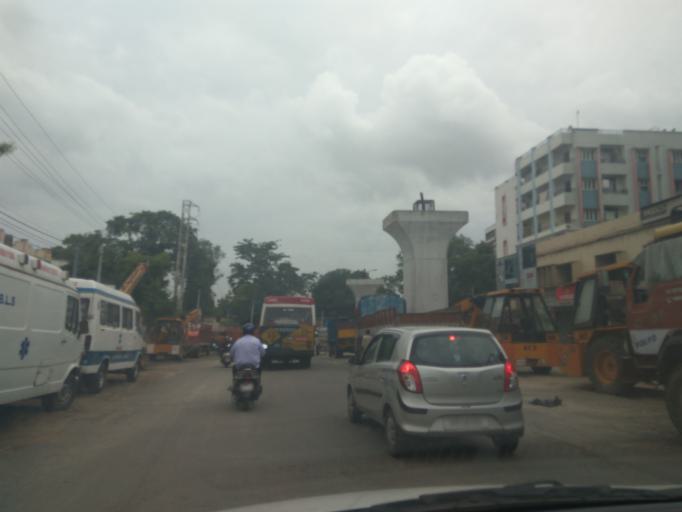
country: IN
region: Telangana
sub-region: Hyderabad
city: Malkajgiri
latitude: 17.4227
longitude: 78.5018
